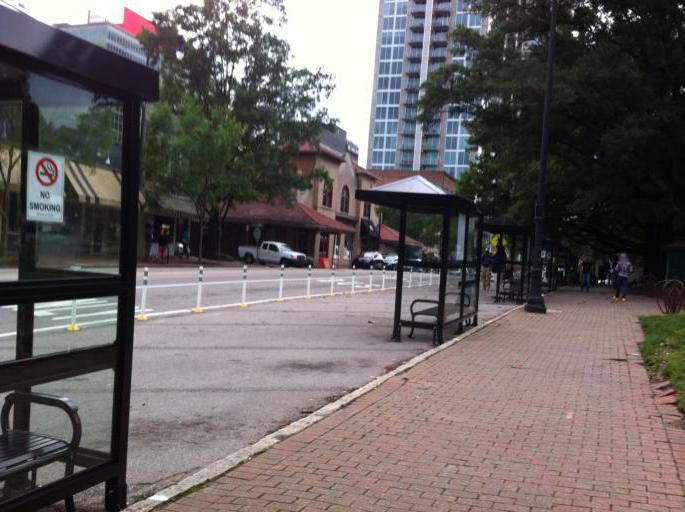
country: US
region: North Carolina
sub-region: Wake County
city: Raleigh
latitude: 35.7769
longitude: -78.6354
